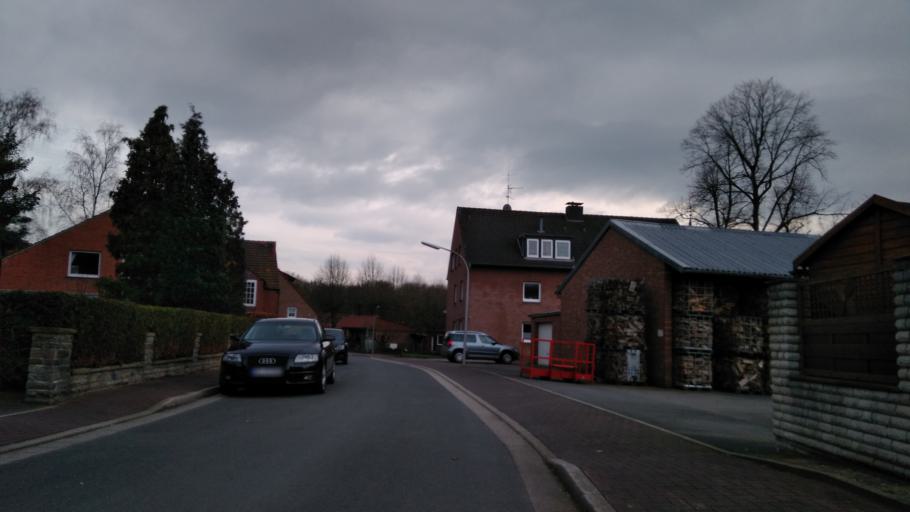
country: DE
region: North Rhine-Westphalia
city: Dorsten
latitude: 51.6746
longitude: 7.0220
